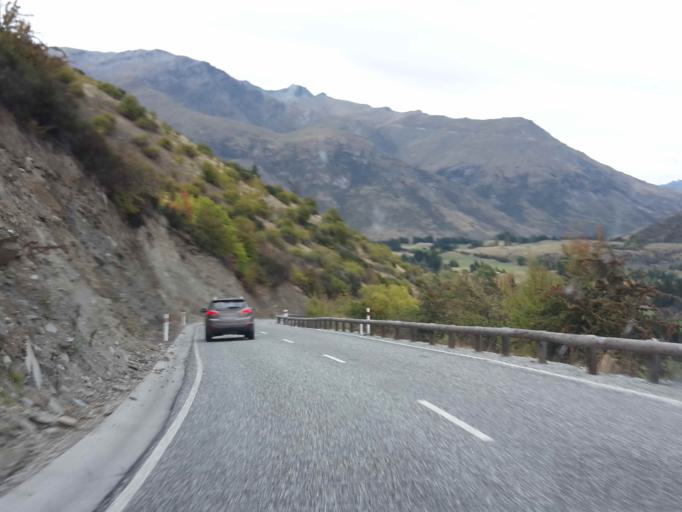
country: NZ
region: Otago
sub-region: Queenstown-Lakes District
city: Arrowtown
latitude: -44.9766
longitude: 168.8600
